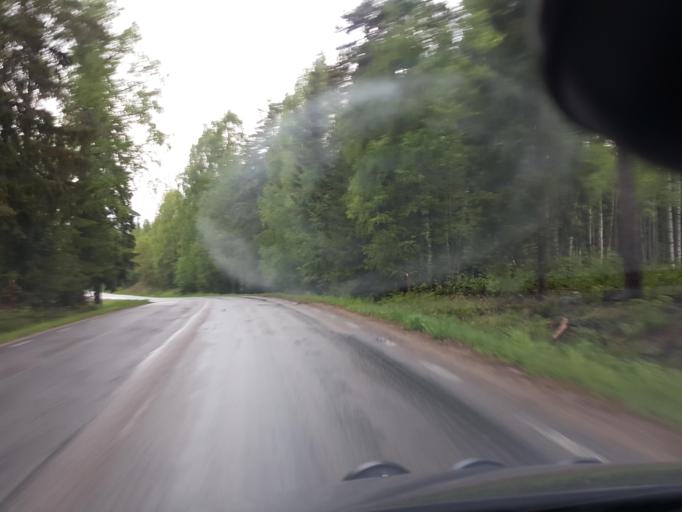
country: SE
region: Gaevleborg
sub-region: Ljusdals Kommun
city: Jaervsoe
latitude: 61.8013
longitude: 16.1731
